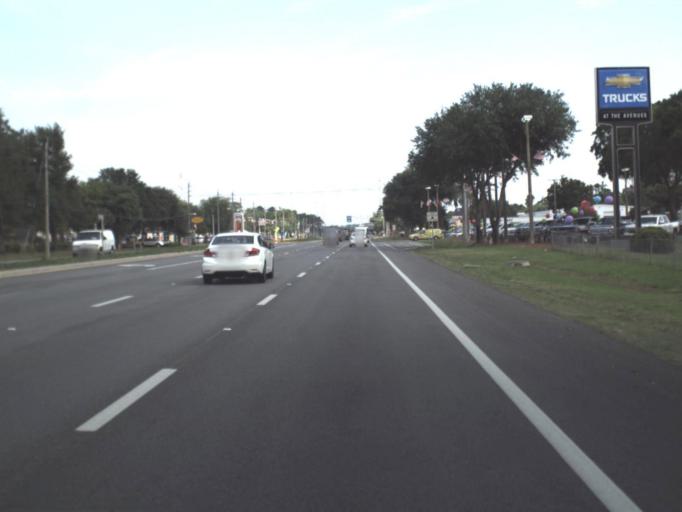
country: US
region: Florida
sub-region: Saint Johns County
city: Fruit Cove
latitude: 30.1743
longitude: -81.5477
